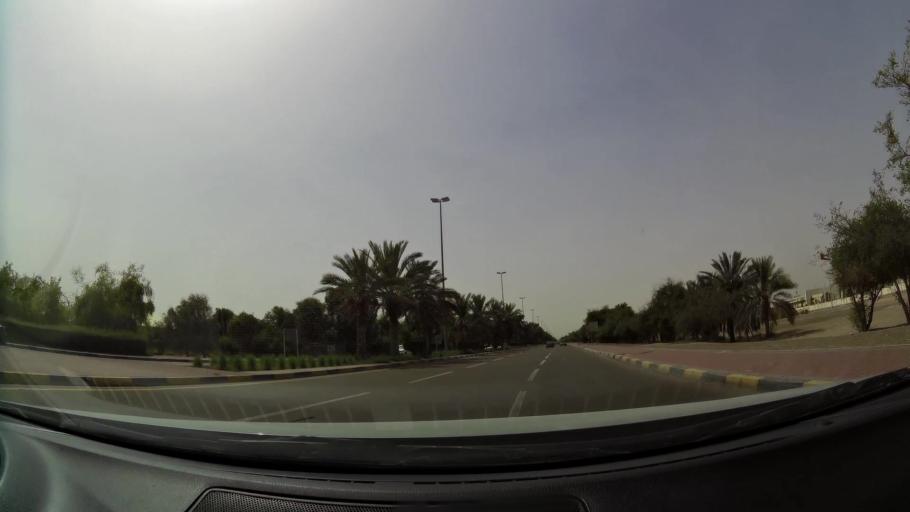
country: AE
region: Abu Dhabi
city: Al Ain
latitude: 24.1759
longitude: 55.6640
